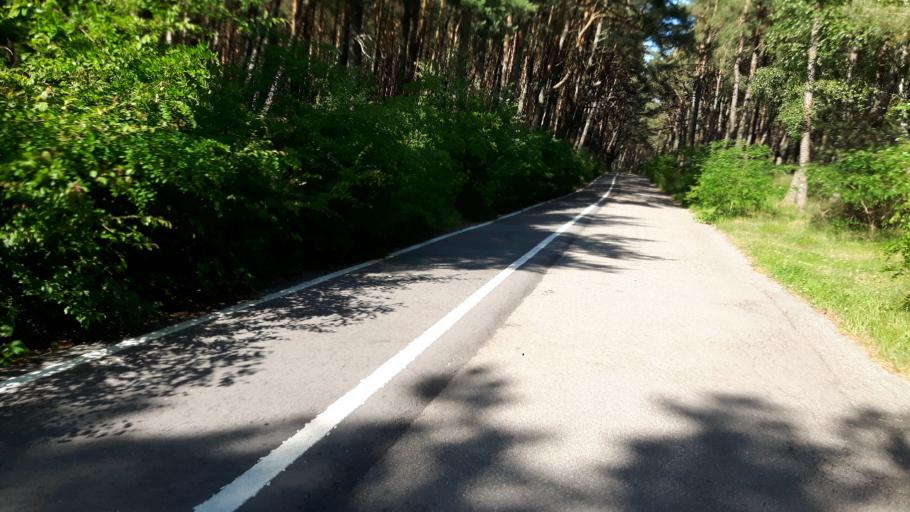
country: LT
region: Klaipedos apskritis
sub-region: Klaipeda
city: Klaipeda
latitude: 55.6995
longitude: 21.1040
